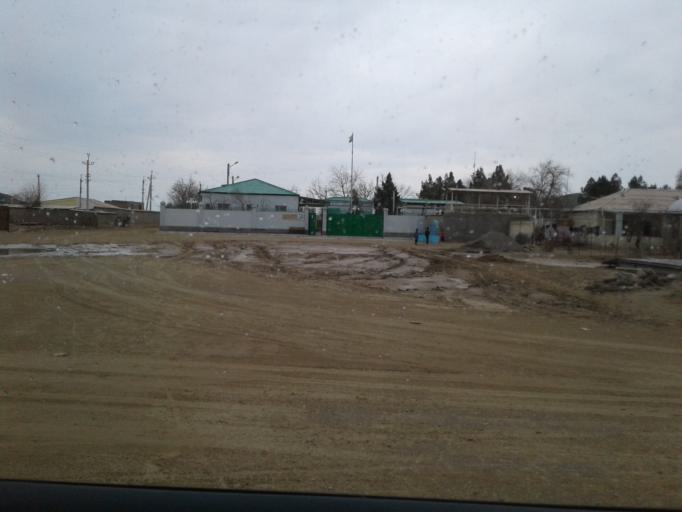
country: TM
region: Ahal
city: Abadan
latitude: 38.7620
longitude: 58.4928
